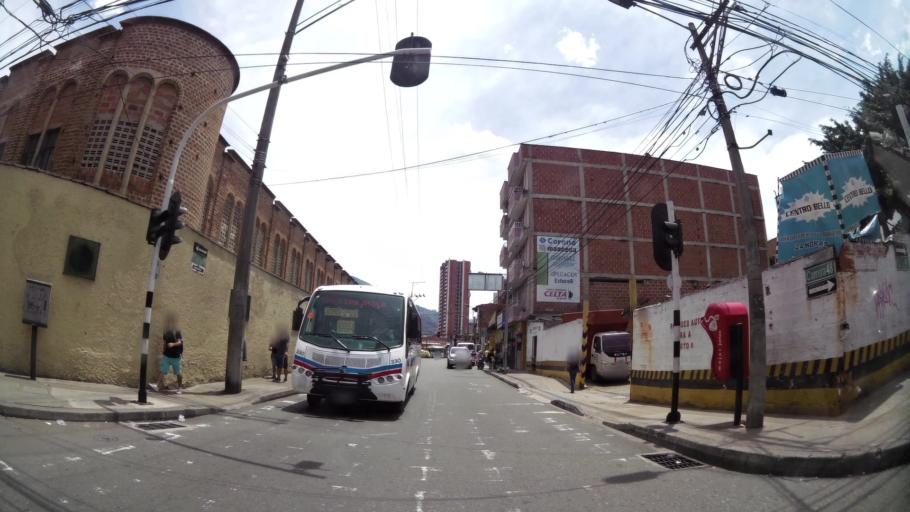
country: CO
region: Antioquia
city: Bello
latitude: 6.3349
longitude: -75.5570
